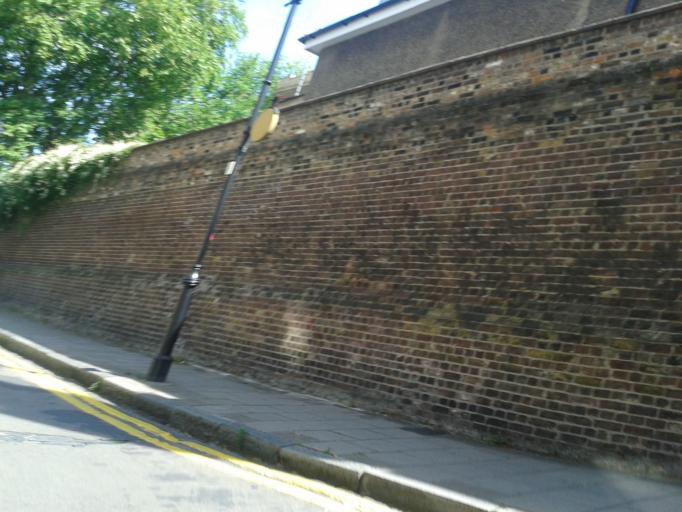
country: GB
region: England
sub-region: Greater London
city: Clerkenwell
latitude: 51.5242
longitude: -0.1064
